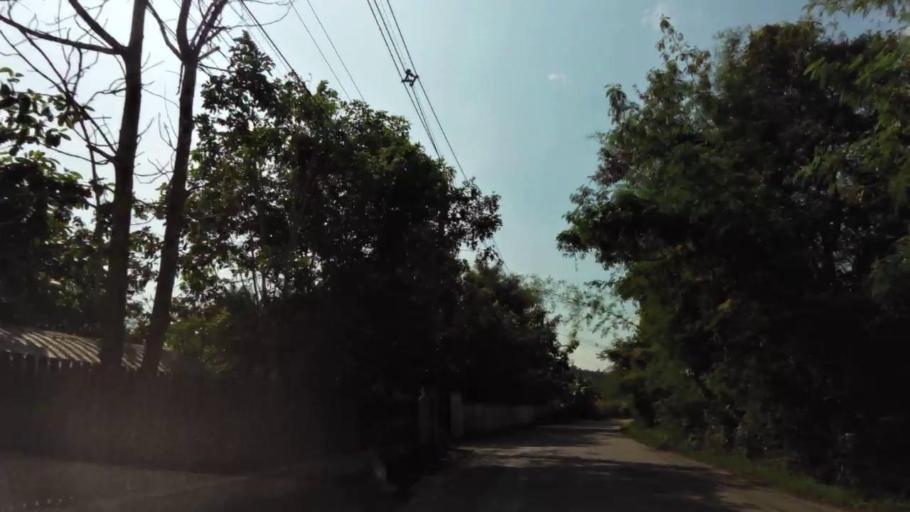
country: TH
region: Chiang Rai
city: Chiang Rai
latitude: 19.8876
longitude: 99.8125
